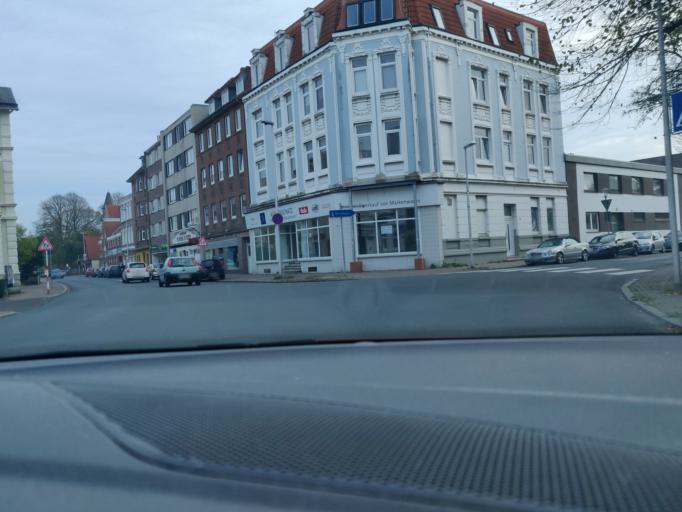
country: DE
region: Lower Saxony
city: Cuxhaven
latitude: 53.8749
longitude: 8.6911
